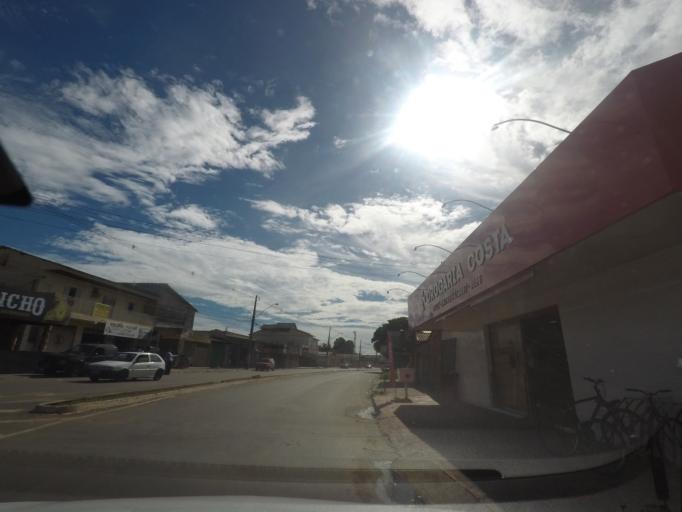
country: BR
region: Goias
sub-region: Aparecida De Goiania
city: Aparecida de Goiania
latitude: -16.8245
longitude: -49.2898
